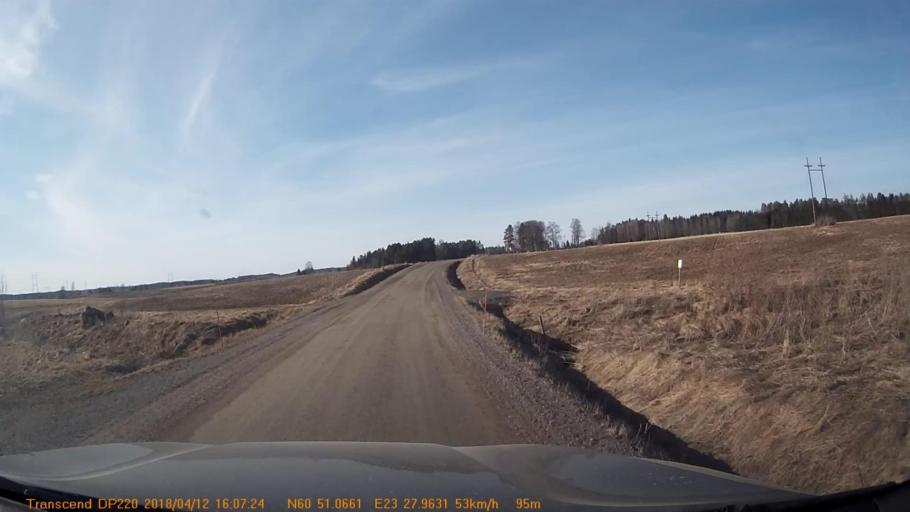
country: FI
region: Haeme
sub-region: Forssa
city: Jokioinen
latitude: 60.8512
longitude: 23.4658
